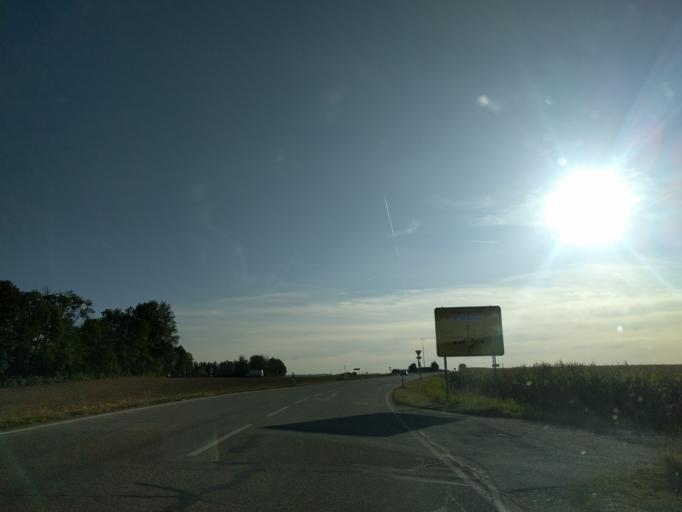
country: DE
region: Bavaria
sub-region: Lower Bavaria
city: Osterhofen
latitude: 48.7143
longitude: 13.0074
